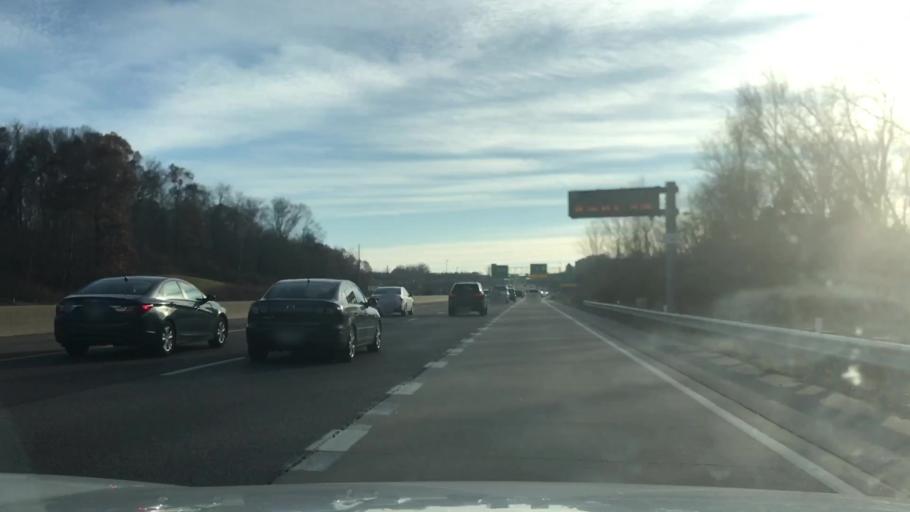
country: US
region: Missouri
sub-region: Saint Louis County
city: Manchester
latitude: 38.6478
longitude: -90.5084
